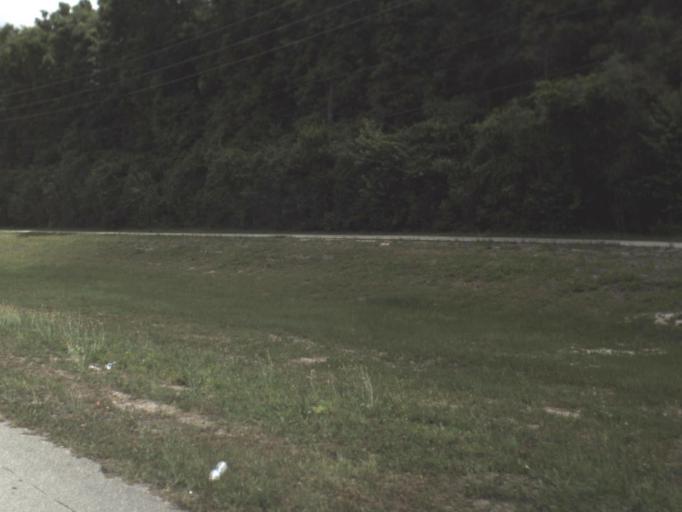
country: US
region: Florida
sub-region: Duval County
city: Jacksonville
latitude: 30.2332
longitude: -81.5519
